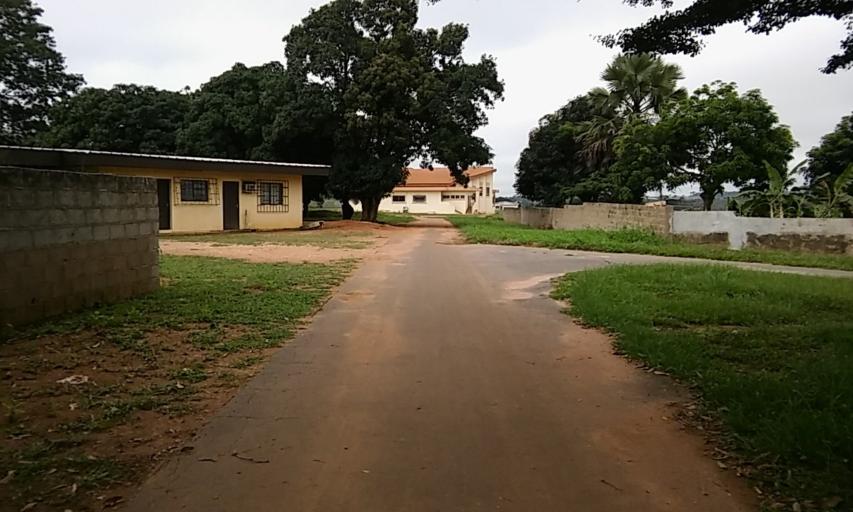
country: CI
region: Vallee du Bandama
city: Bouake
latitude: 7.6909
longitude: -5.0620
